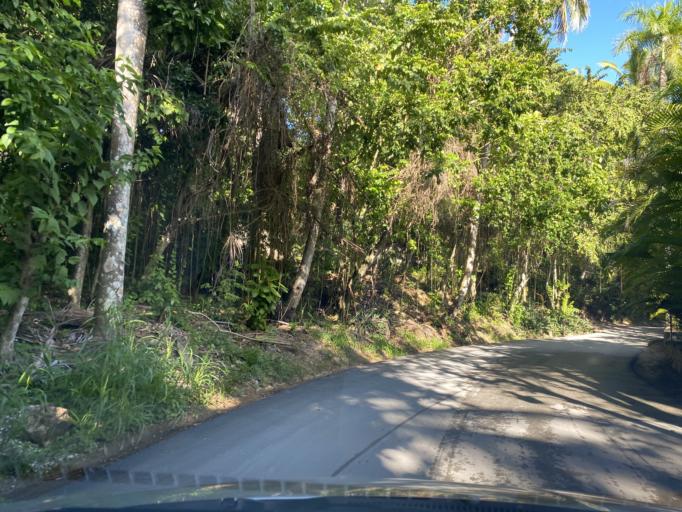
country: DO
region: Samana
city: Las Terrenas
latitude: 19.3185
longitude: -69.5591
